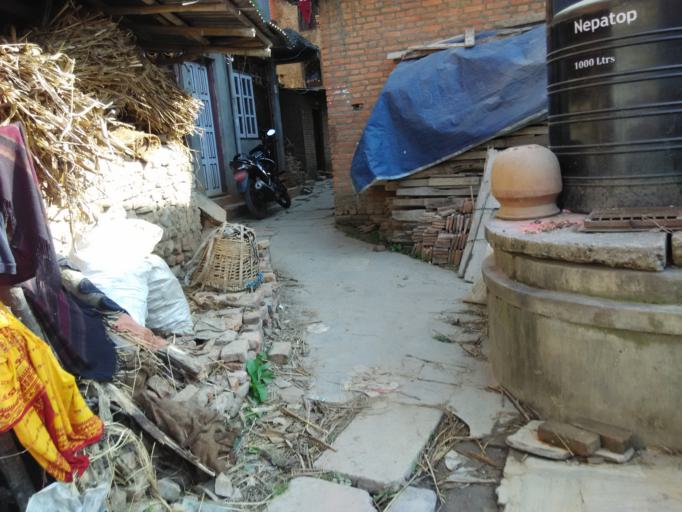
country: NP
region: Central Region
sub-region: Bagmati Zone
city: Patan
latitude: 27.6283
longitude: 85.3027
